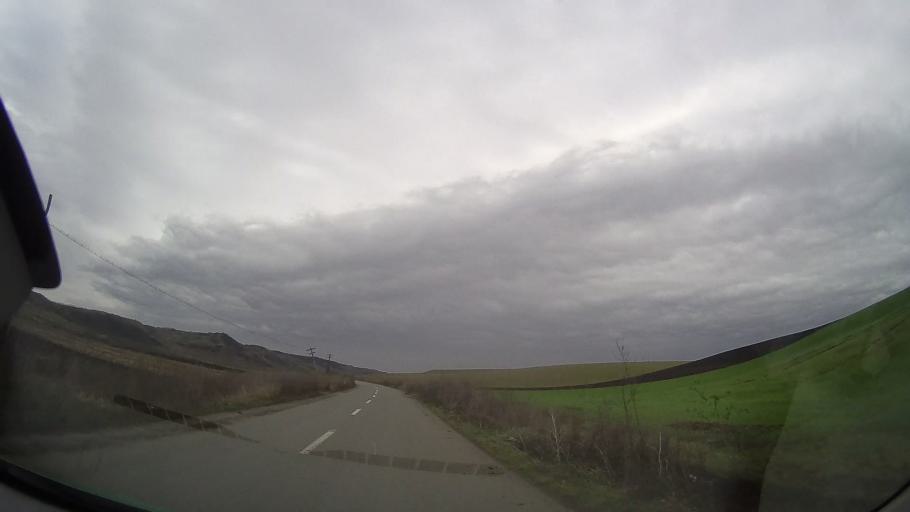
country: RO
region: Bistrita-Nasaud
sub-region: Comuna Milas
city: Milas
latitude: 46.7895
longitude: 24.4220
